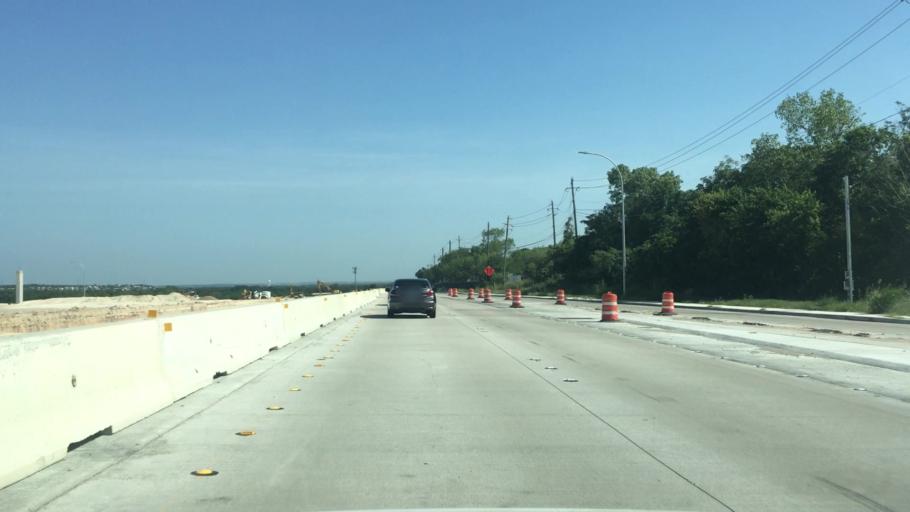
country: US
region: Texas
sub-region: Travis County
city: Austin
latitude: 30.3111
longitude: -97.6623
